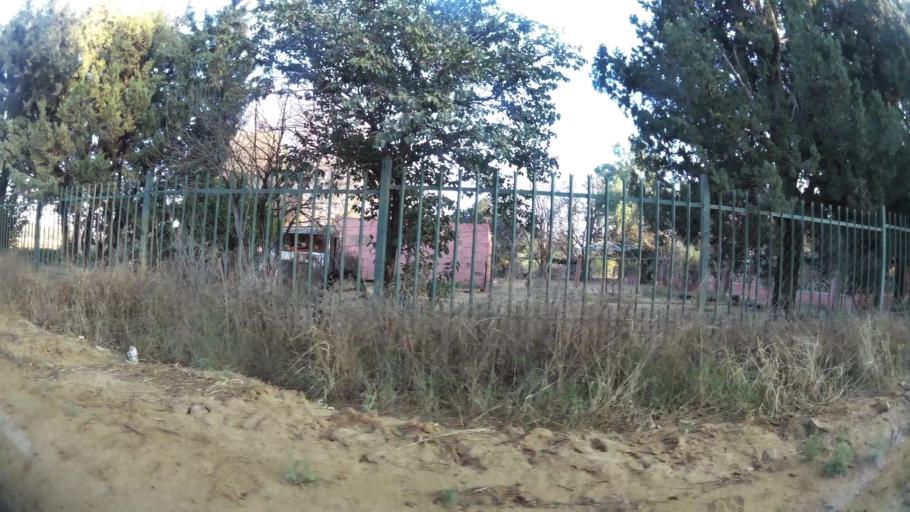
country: ZA
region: Orange Free State
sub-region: Mangaung Metropolitan Municipality
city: Bloemfontein
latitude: -29.0888
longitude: 26.1416
